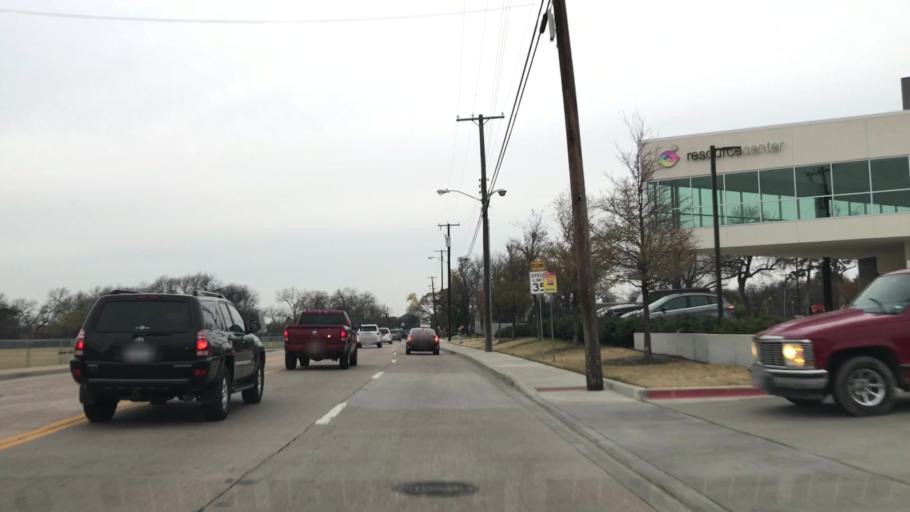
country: US
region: Texas
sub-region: Dallas County
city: University Park
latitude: 32.8262
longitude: -96.8316
